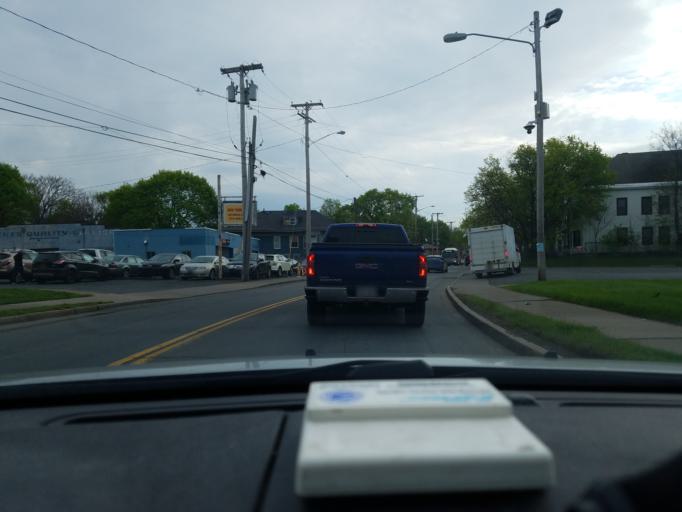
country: US
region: New York
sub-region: Onondaga County
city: Syracuse
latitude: 43.0255
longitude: -76.1449
